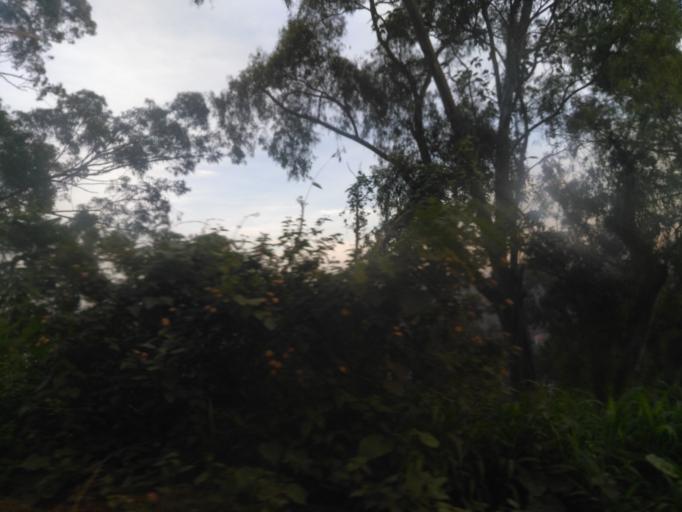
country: UG
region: Central Region
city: Kampala Central Division
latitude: 0.3403
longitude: 32.5799
